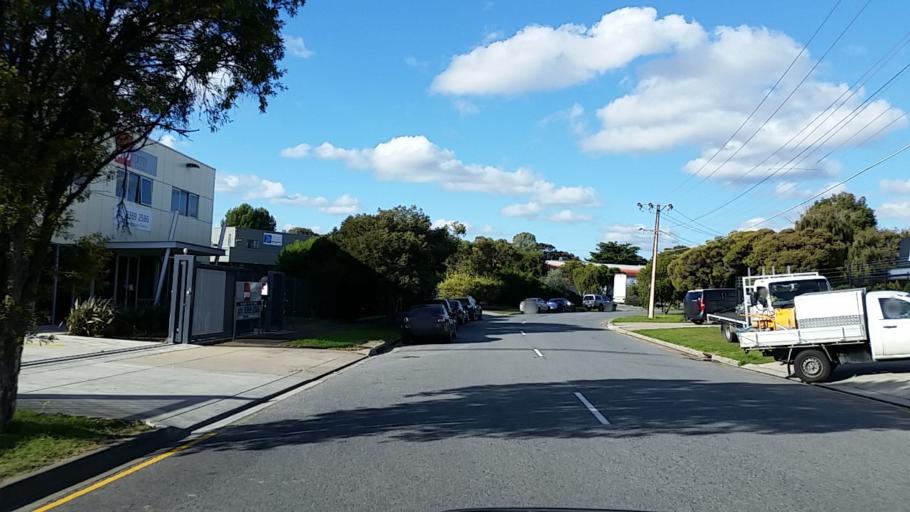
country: AU
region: South Australia
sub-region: Tea Tree Gully
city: Modbury
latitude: -34.8460
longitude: 138.6744
